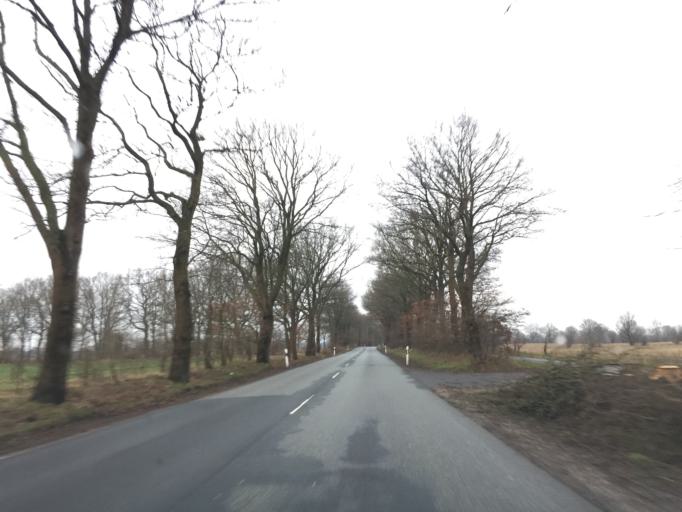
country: DE
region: Schleswig-Holstein
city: Wahlstedt
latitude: 53.9622
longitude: 10.1933
